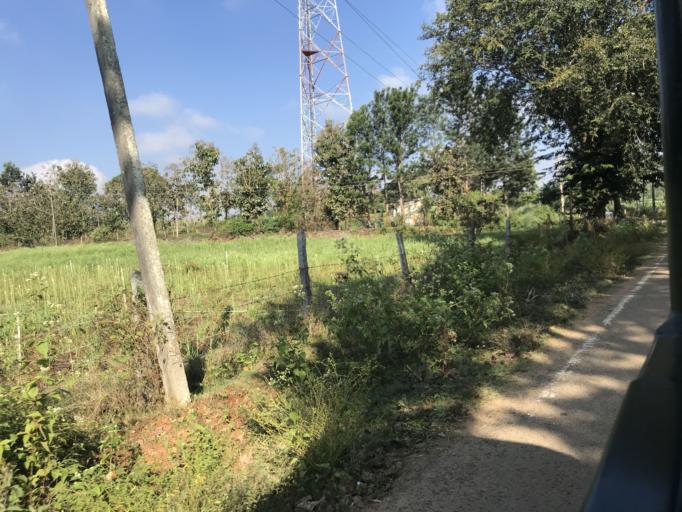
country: IN
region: Karnataka
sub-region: Mysore
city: Sargur
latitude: 11.9418
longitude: 76.2689
